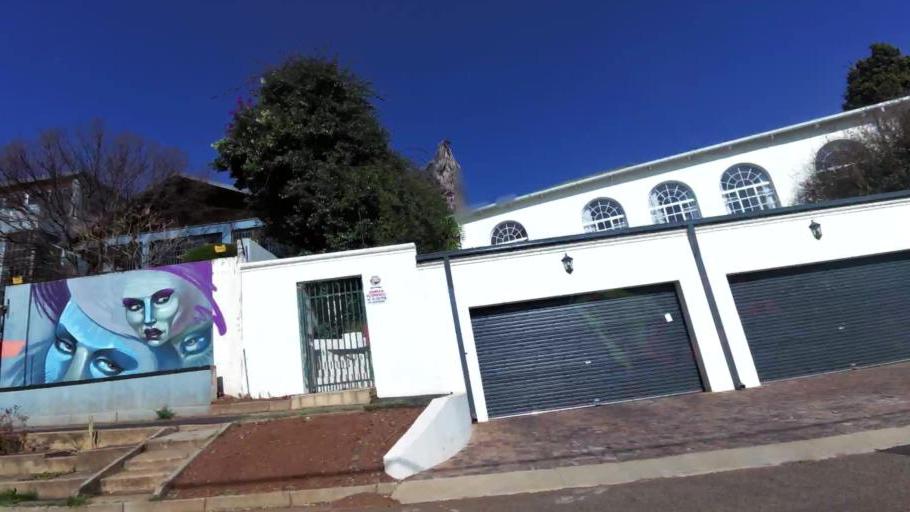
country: ZA
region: Gauteng
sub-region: City of Johannesburg Metropolitan Municipality
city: Johannesburg
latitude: -26.1770
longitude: 27.9963
